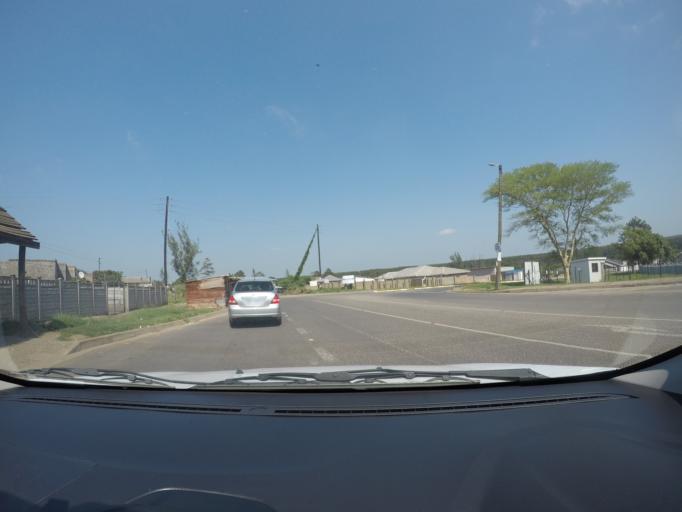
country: ZA
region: KwaZulu-Natal
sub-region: uThungulu District Municipality
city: eSikhawini
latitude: -28.8927
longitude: 31.8813
